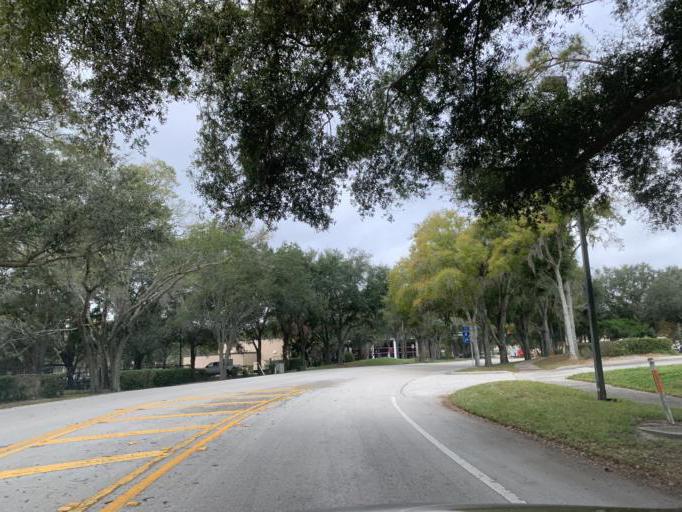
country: US
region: Florida
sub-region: Orange County
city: Eatonville
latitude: 28.6294
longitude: -81.3917
